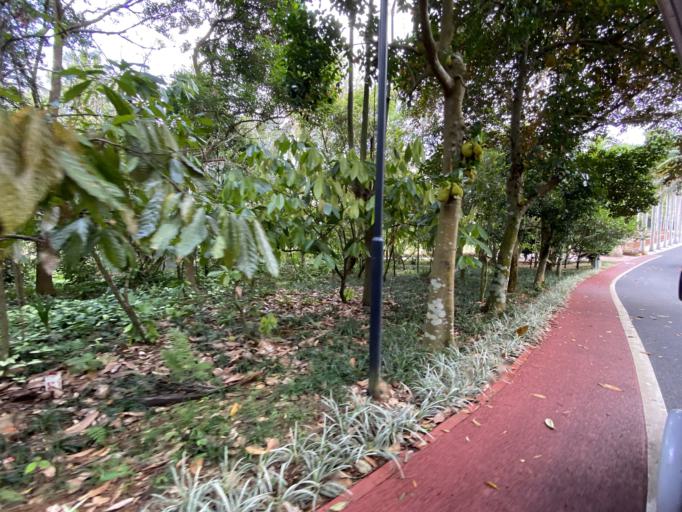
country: CN
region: Hainan
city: Nanqiao
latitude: 18.7329
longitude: 110.1905
